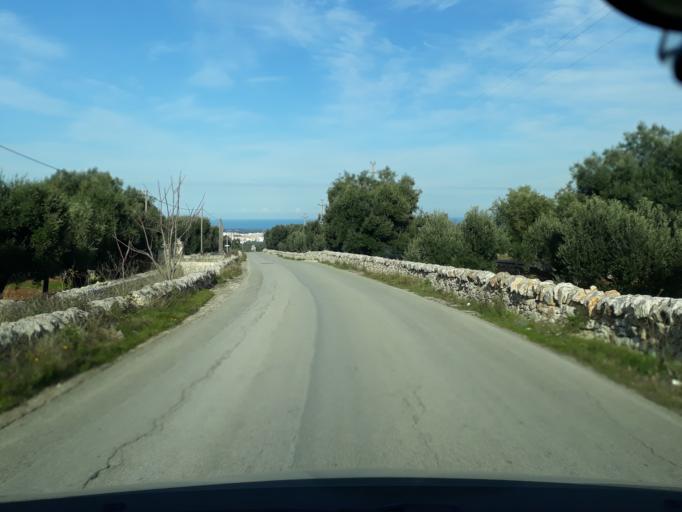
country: IT
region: Apulia
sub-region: Provincia di Brindisi
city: Lamie di Olimpie-Selva
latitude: 40.8094
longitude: 17.3549
